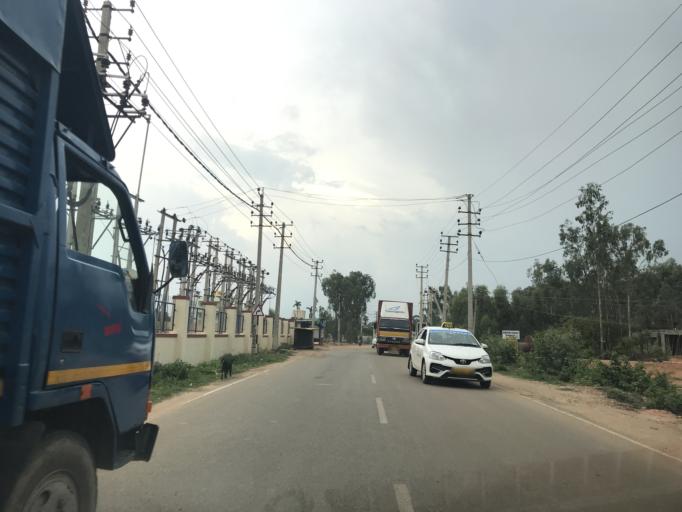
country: IN
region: Karnataka
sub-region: Bangalore Rural
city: Devanhalli
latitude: 13.1829
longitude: 77.6771
